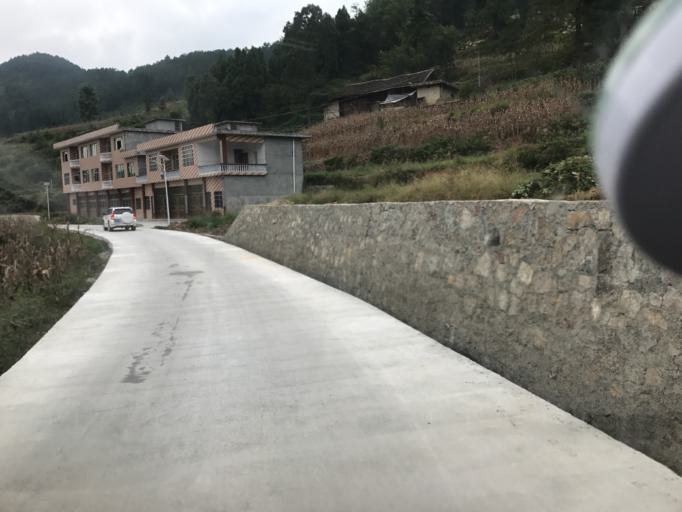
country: CN
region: Guizhou Sheng
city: Donghua
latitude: 28.0680
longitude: 108.0852
